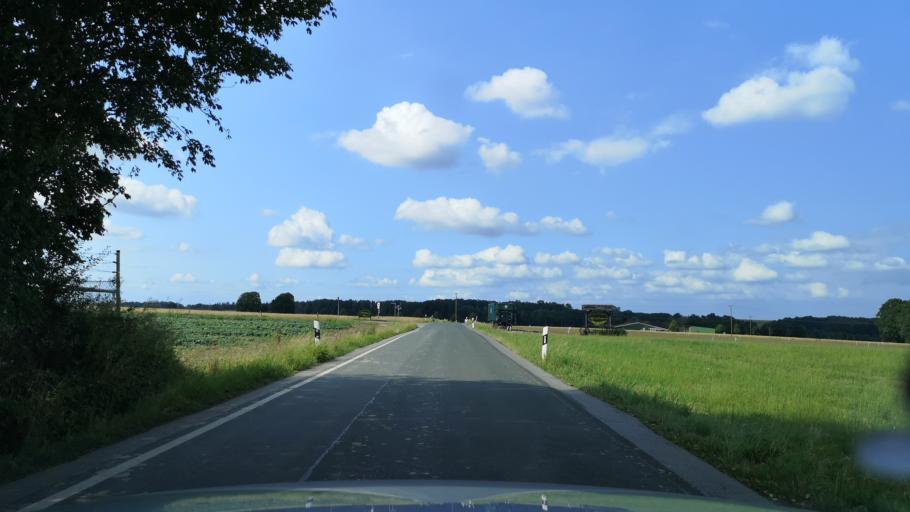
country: DE
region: North Rhine-Westphalia
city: Iserlohn
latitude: 51.4320
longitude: 7.7094
